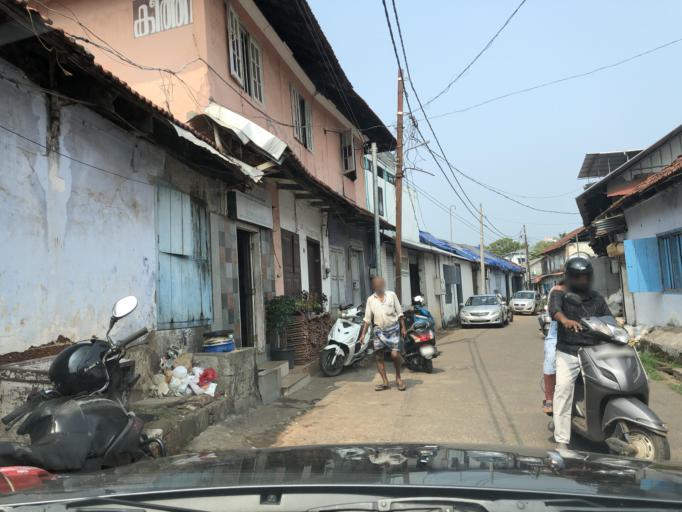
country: IN
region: Kerala
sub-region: Kozhikode
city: Kozhikode
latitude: 11.2500
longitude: 75.7754
